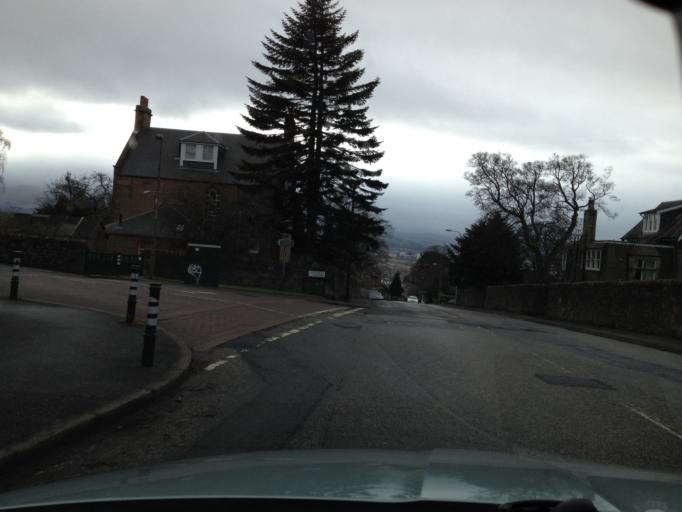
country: GB
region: Scotland
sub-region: Edinburgh
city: Colinton
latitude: 55.9484
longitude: -3.2796
